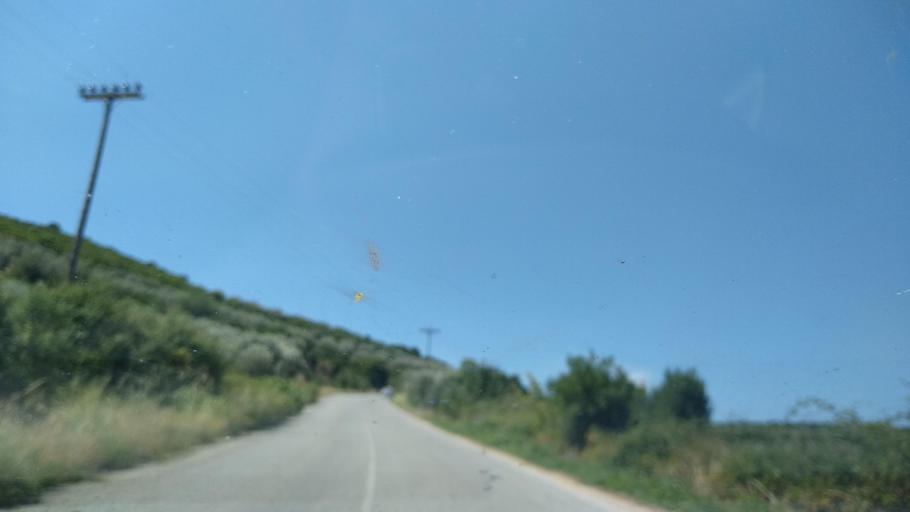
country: GR
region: Central Macedonia
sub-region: Nomos Chalkidikis
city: Megali Panagia
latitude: 40.3486
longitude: 23.6580
